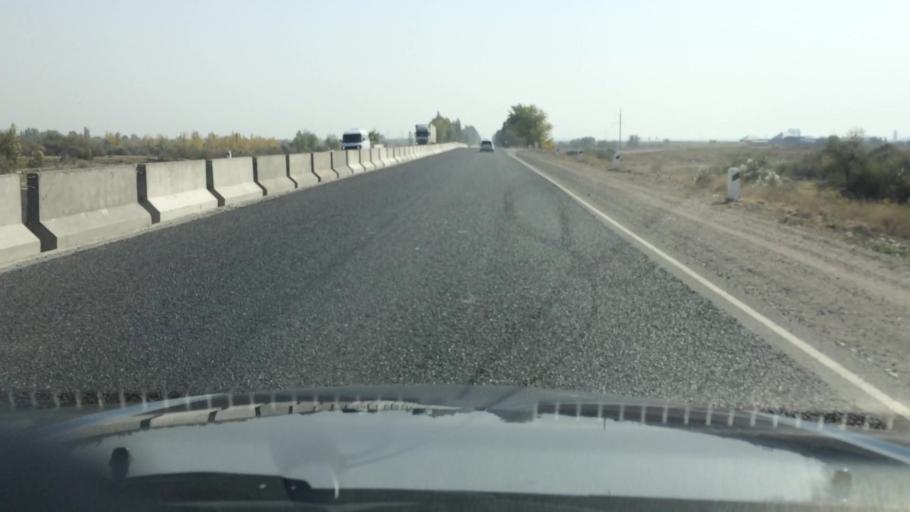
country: KG
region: Chuy
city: Kant
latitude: 42.9709
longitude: 74.9020
